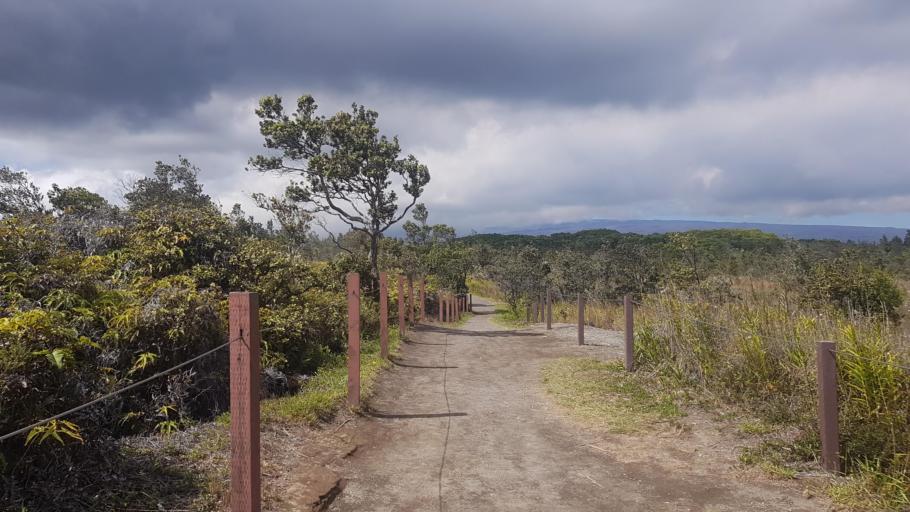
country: US
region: Hawaii
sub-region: Hawaii County
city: Volcano
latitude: 19.4301
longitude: -155.2683
